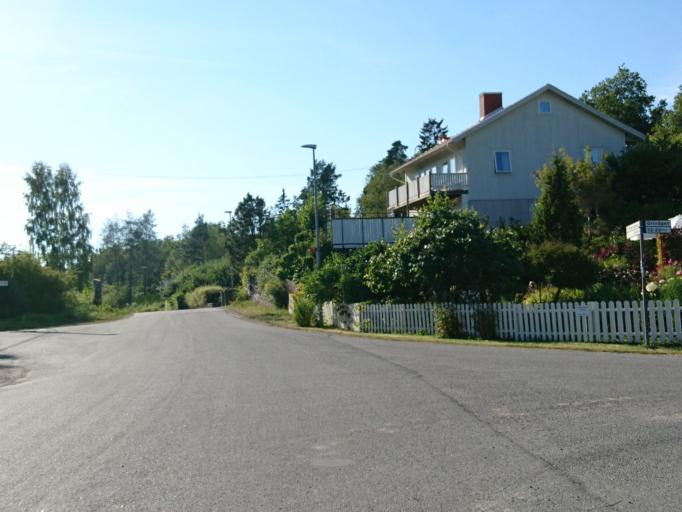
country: SE
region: Stockholm
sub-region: Huddinge Kommun
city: Segeltorp
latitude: 59.2680
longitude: 17.9493
